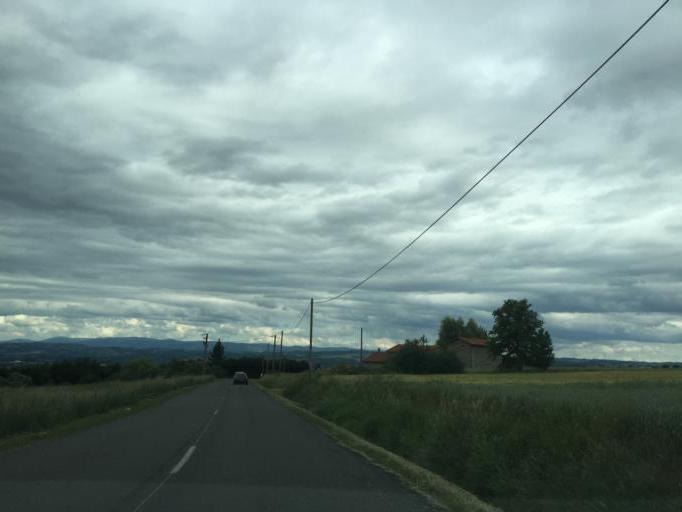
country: FR
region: Rhone-Alpes
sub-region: Departement de la Loire
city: Saint-Georges-Haute-Ville
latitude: 45.5104
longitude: 4.1114
